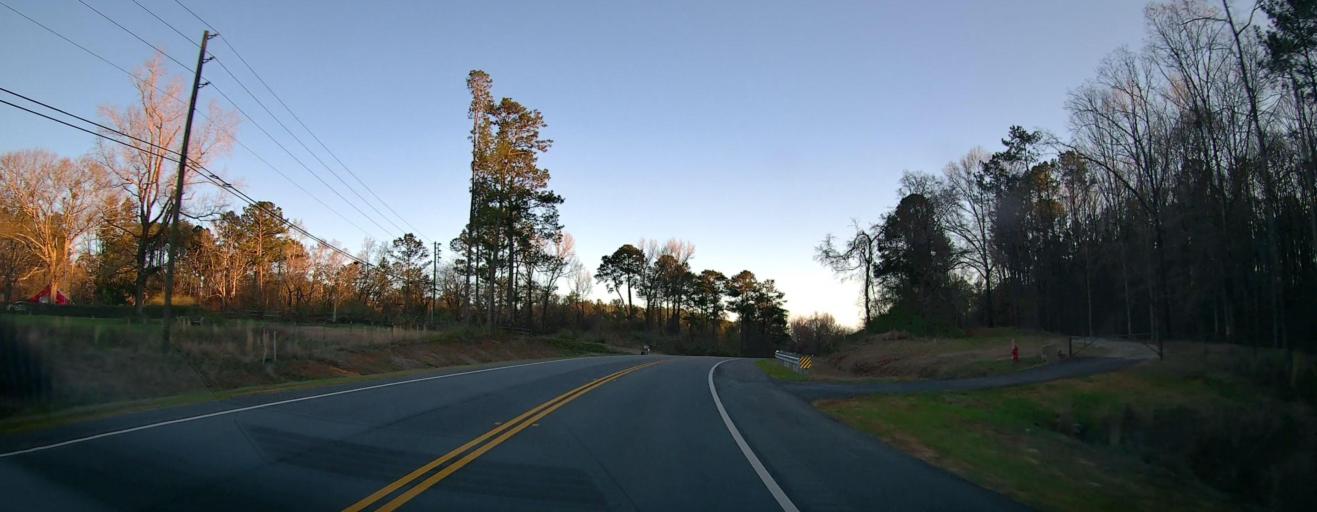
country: US
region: Alabama
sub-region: Lee County
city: Smiths Station
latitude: 32.6170
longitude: -85.0271
